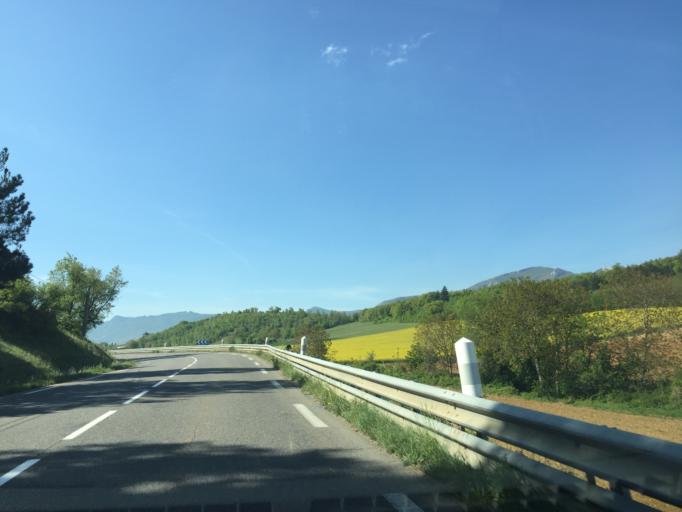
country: FR
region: Provence-Alpes-Cote d'Azur
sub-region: Departement des Hautes-Alpes
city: Laragne-Monteglin
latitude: 44.2835
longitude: 5.8469
